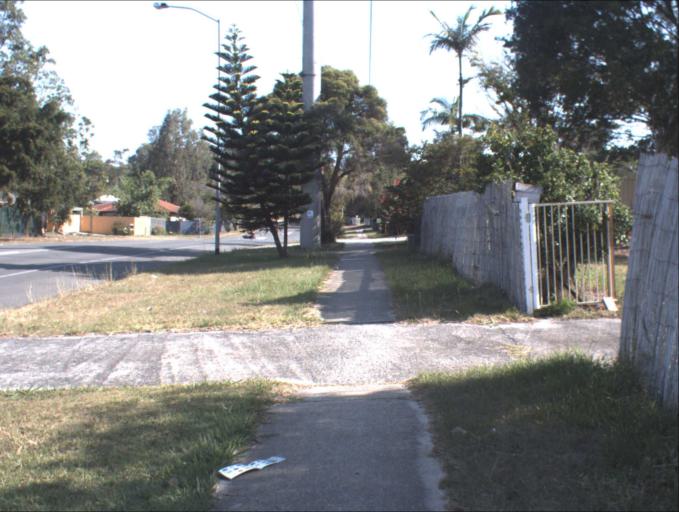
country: AU
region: Queensland
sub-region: Logan
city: Beenleigh
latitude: -27.6918
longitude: 153.1792
